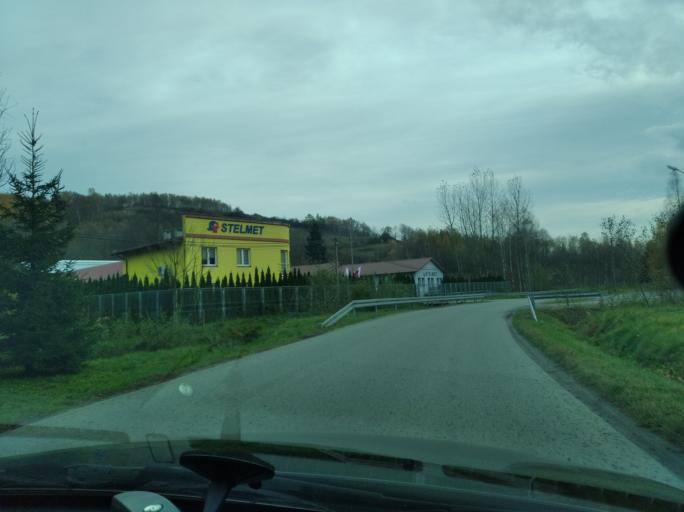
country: PL
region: Subcarpathian Voivodeship
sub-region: Powiat ropczycko-sedziszowski
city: Iwierzyce
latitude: 49.9472
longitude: 21.7495
